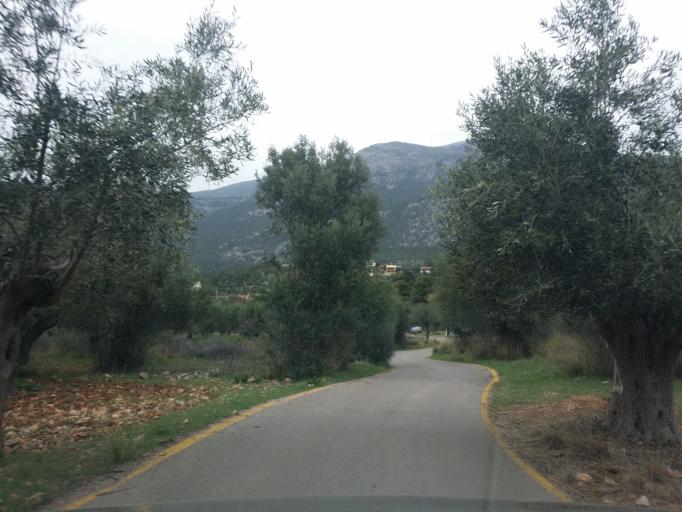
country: GR
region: Central Greece
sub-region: Nomos Voiotias
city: Kaparellion
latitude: 38.1469
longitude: 23.2308
